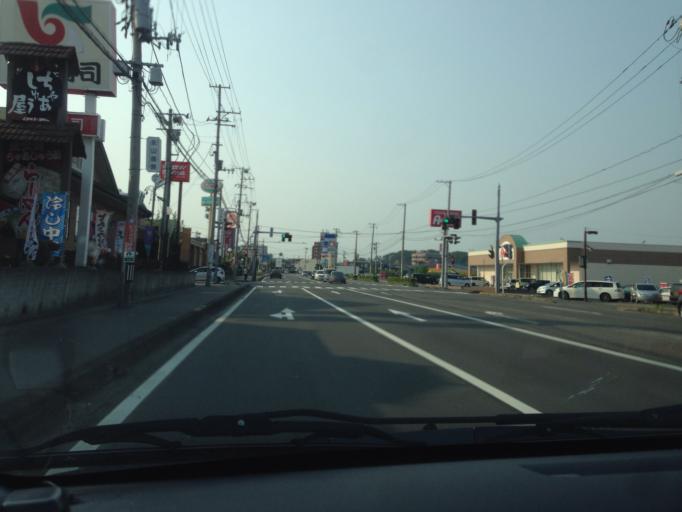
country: JP
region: Tochigi
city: Kuroiso
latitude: 37.1182
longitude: 140.1954
